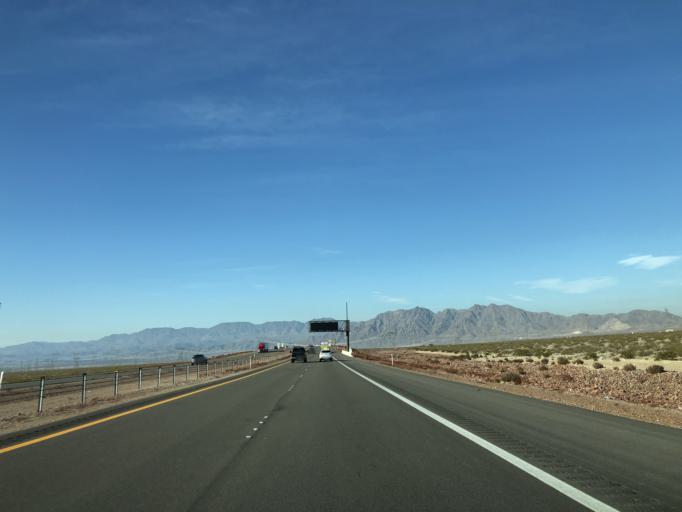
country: US
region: Nevada
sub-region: Clark County
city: Boulder City
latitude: 35.9345
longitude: -114.8362
